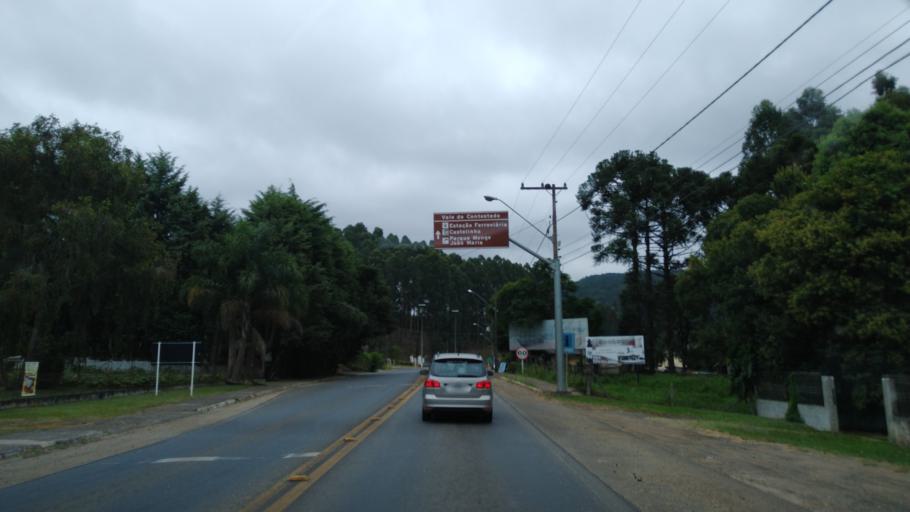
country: BR
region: Santa Catarina
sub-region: Porto Uniao
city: Porto Uniao
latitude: -26.2819
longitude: -51.0477
